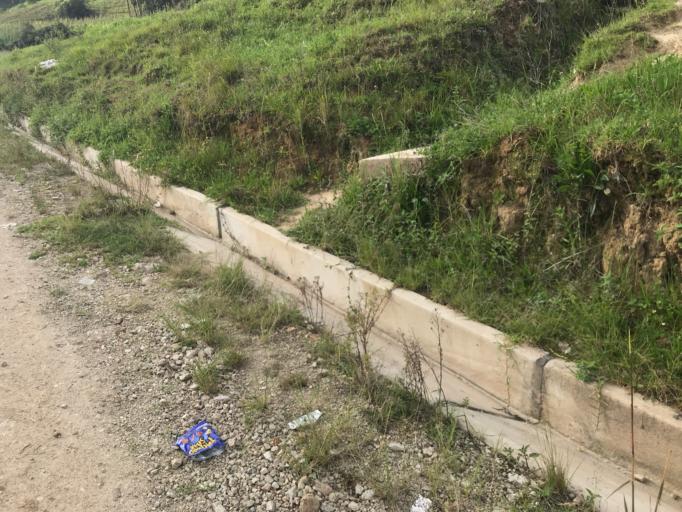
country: PE
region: Cajamarca
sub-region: Provincia de Chota
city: Querocoto
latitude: -6.3567
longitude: -79.0347
